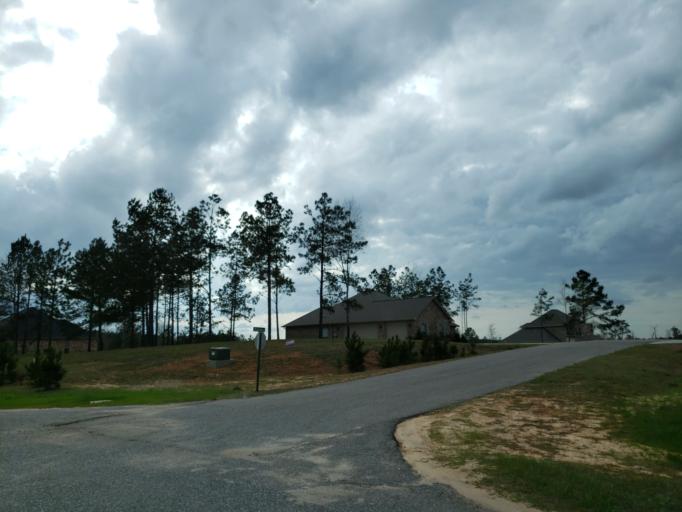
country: US
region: Mississippi
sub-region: Jones County
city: Ellisville
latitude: 31.5538
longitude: -89.2585
